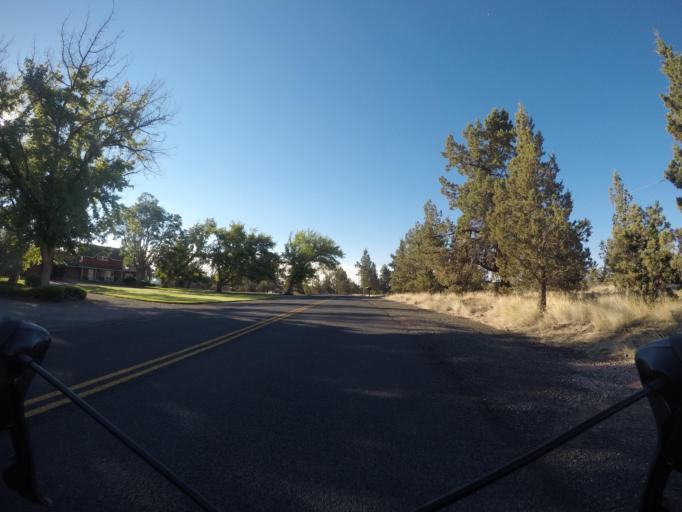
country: US
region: Oregon
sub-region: Deschutes County
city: Redmond
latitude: 44.2666
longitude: -121.2491
